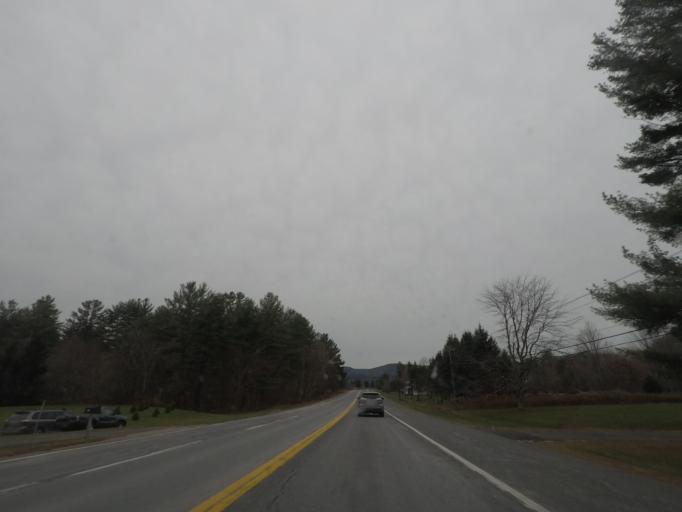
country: US
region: Massachusetts
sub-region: Berkshire County
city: Lanesborough
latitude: 42.5450
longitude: -73.3532
